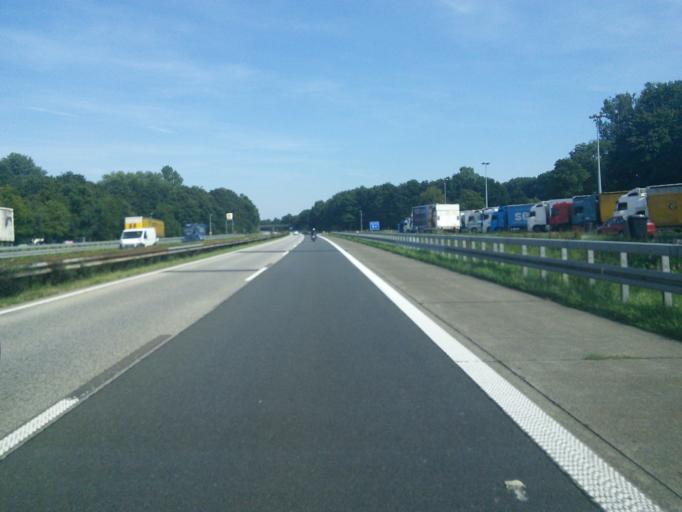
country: DE
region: North Rhine-Westphalia
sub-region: Regierungsbezirk Dusseldorf
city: Willich
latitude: 51.2370
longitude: 6.5124
